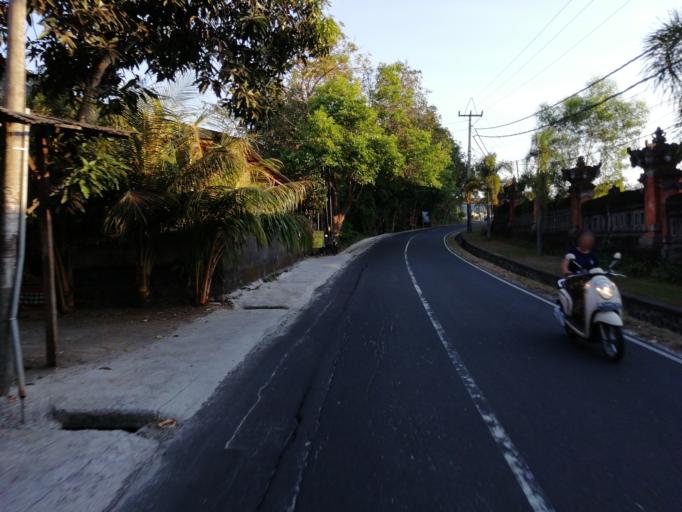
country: ID
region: Bali
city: Bualu
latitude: -8.8147
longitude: 115.1922
